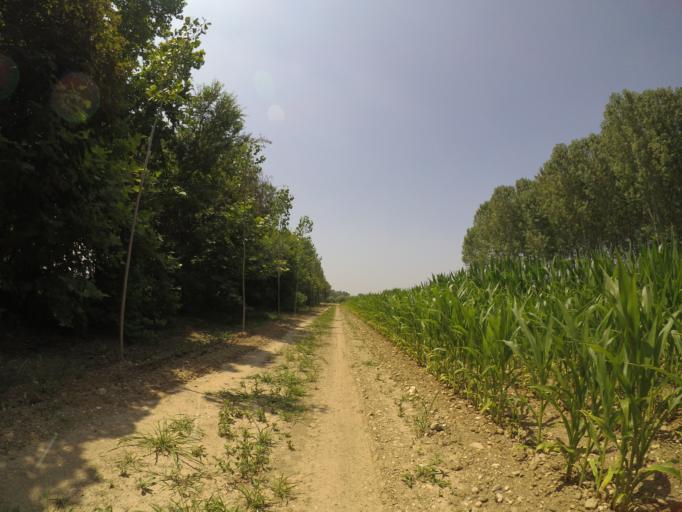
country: IT
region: Friuli Venezia Giulia
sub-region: Provincia di Udine
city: Bertiolo
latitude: 45.9282
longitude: 13.0519
